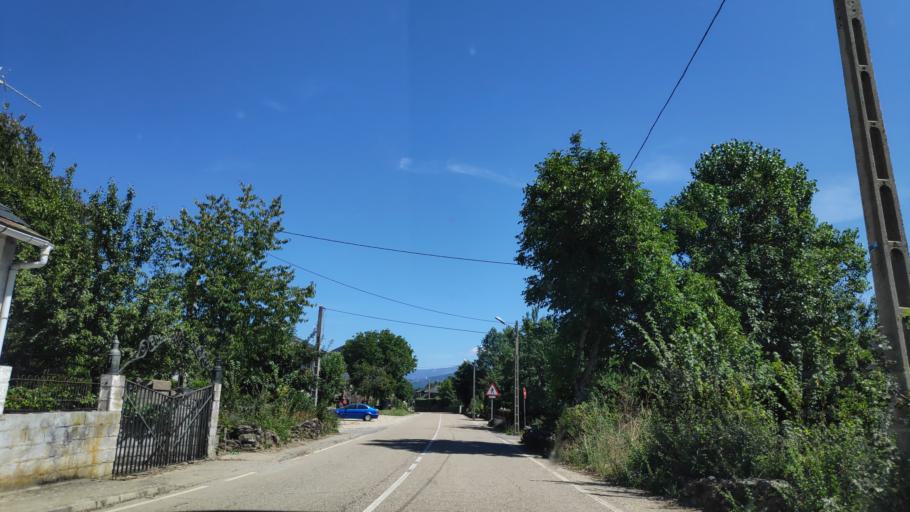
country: ES
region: Castille and Leon
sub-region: Provincia de Zamora
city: Puebla de Sanabria
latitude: 42.0374
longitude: -6.6685
